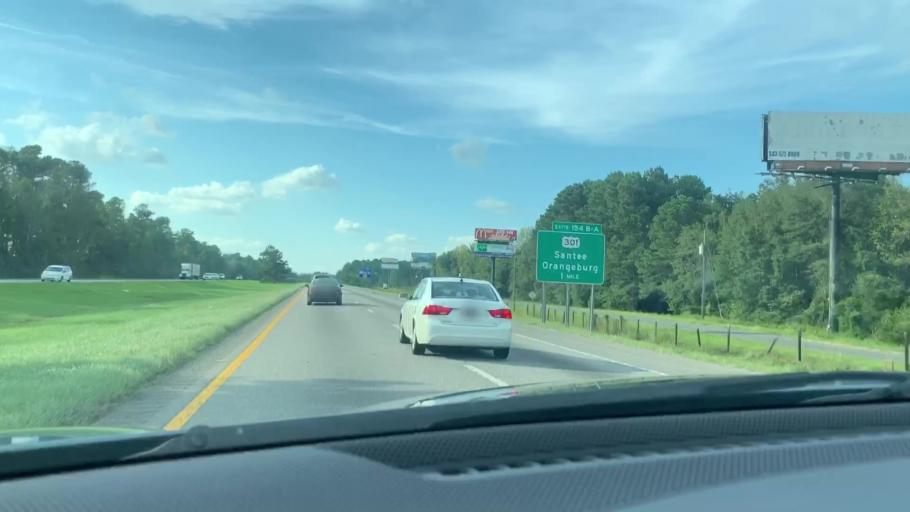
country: US
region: South Carolina
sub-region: Orangeburg County
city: Brookdale
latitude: 33.4465
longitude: -80.7151
